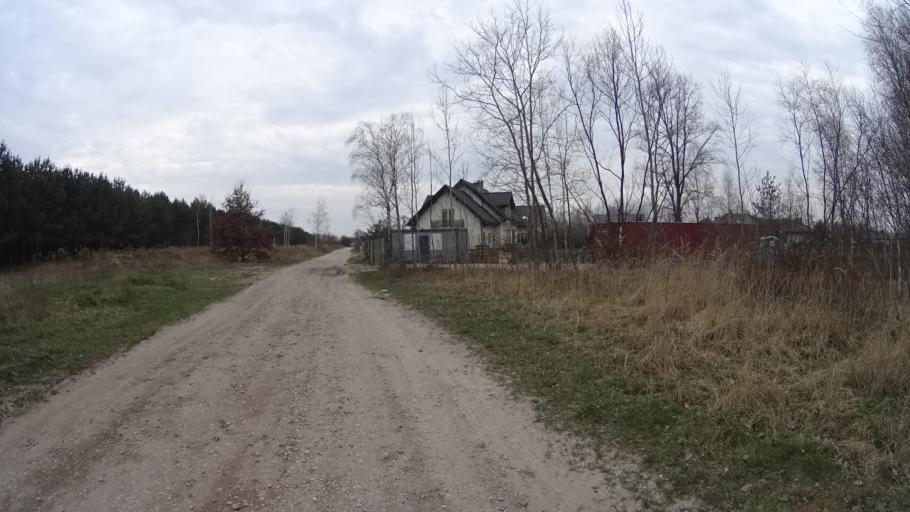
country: PL
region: Masovian Voivodeship
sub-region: Powiat warszawski zachodni
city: Jozefow
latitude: 52.2458
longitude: 20.6873
